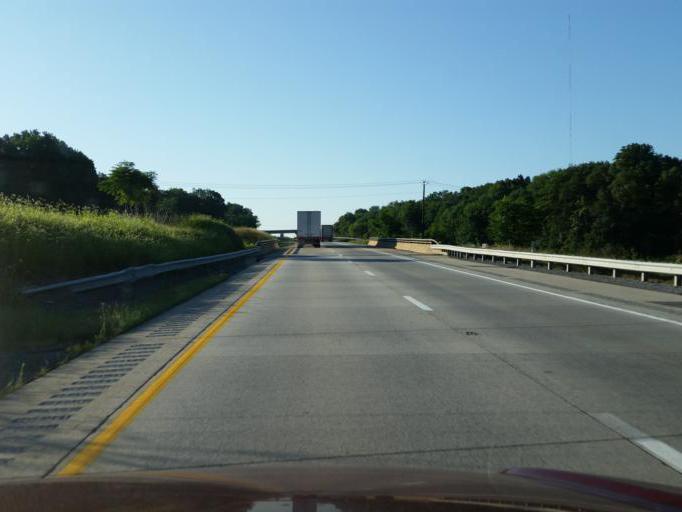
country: US
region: Pennsylvania
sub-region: Lancaster County
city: Elizabethtown
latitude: 40.1785
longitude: -76.6017
